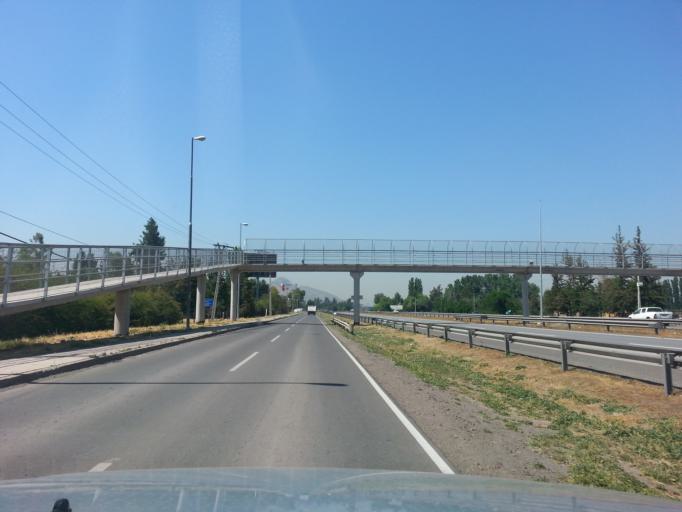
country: CL
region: Santiago Metropolitan
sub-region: Provincia de Chacabuco
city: Chicureo Abajo
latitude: -33.2502
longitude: -70.6977
